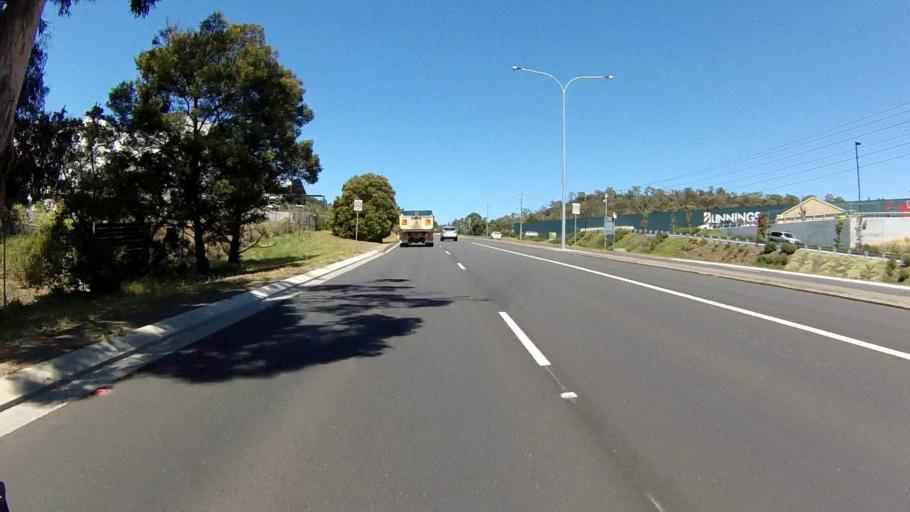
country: AU
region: Tasmania
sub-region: Clarence
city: Warrane
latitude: -42.8607
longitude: 147.3939
